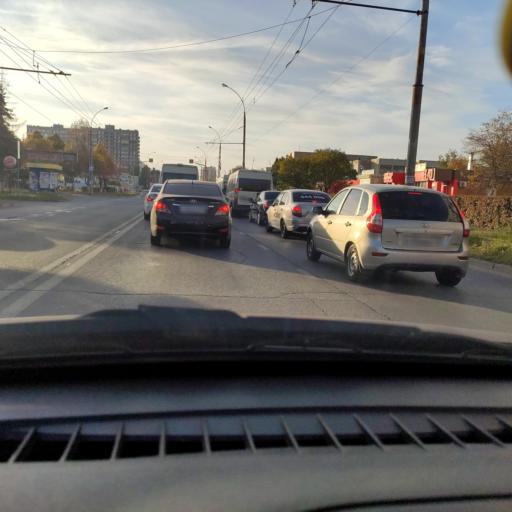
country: RU
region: Samara
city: Tol'yatti
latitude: 53.5347
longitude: 49.3163
